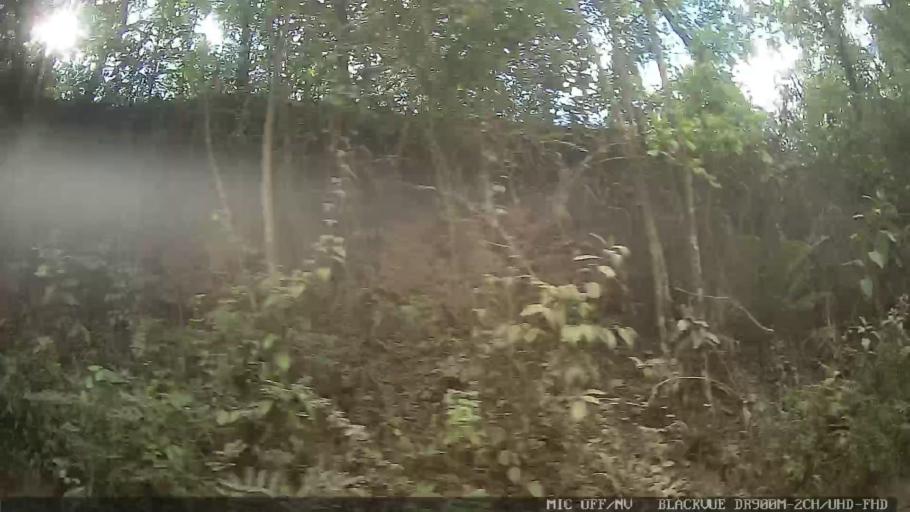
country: BR
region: Sao Paulo
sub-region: Bom Jesus Dos Perdoes
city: Bom Jesus dos Perdoes
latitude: -23.1381
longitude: -46.5081
